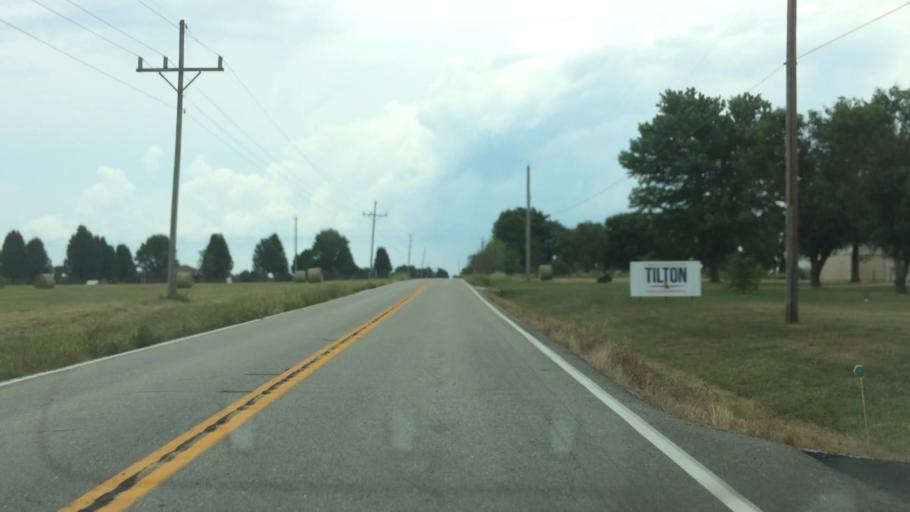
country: US
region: Missouri
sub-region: Greene County
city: Strafford
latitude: 37.2454
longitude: -93.1354
